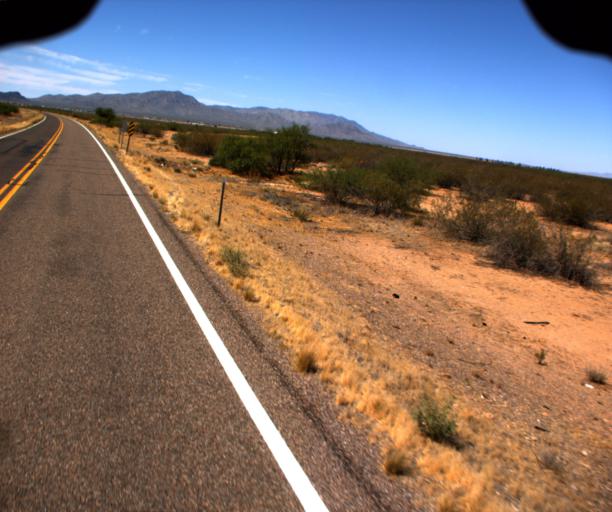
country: US
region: Arizona
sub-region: Yavapai County
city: Congress
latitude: 33.9841
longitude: -113.1380
